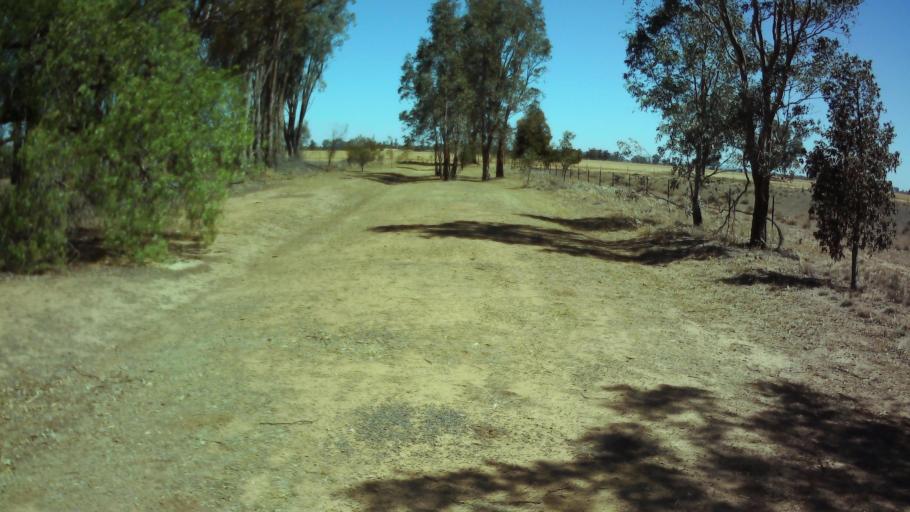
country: AU
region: New South Wales
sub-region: Weddin
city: Grenfell
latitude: -34.0160
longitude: 147.7896
